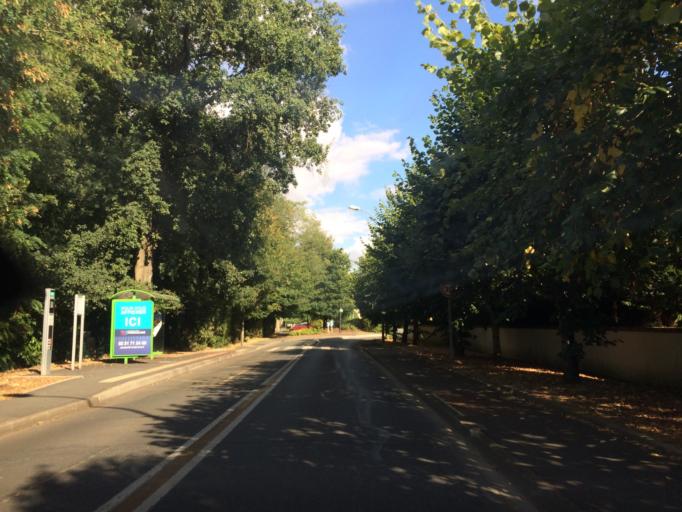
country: FR
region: Ile-de-France
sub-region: Departement de l'Essonne
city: Marolles-en-Hurepoix
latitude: 48.5600
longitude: 2.3094
